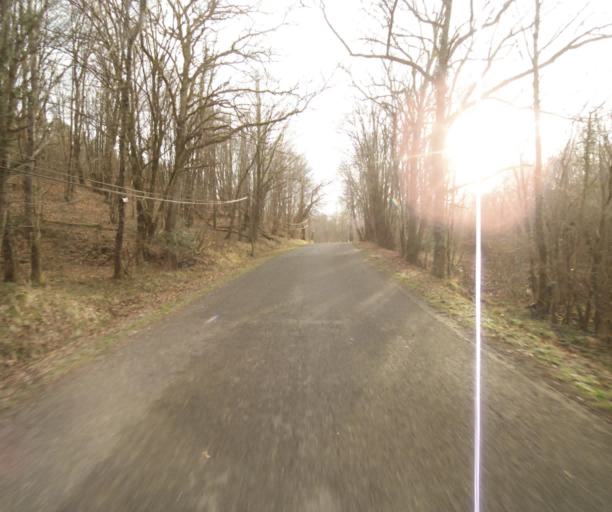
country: FR
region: Aquitaine
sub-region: Departement des Landes
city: Gabarret
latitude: 44.0182
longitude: 0.0464
